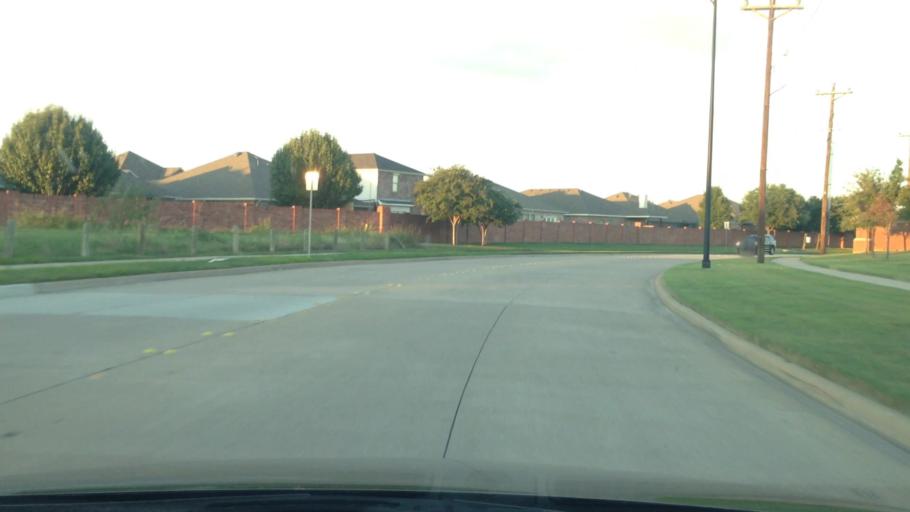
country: US
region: Texas
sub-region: Denton County
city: Little Elm
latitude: 33.1407
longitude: -96.9223
